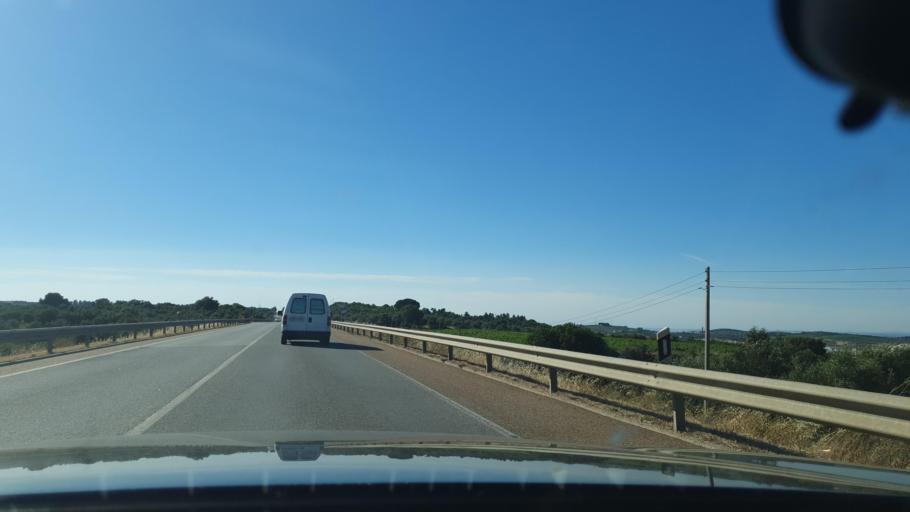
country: PT
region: Evora
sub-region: Borba
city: Borba
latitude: 38.7841
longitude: -7.4494
